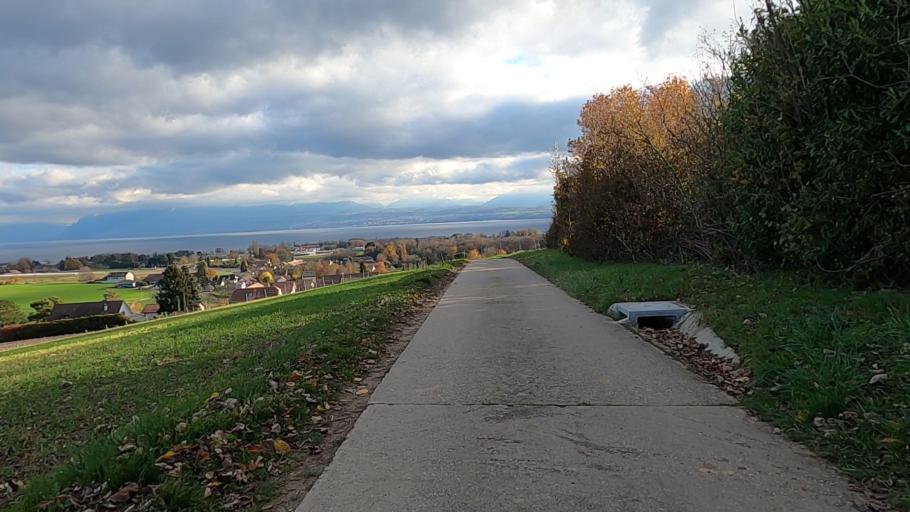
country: CH
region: Vaud
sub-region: Morges District
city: Saint-Prex
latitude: 46.5095
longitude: 6.4583
